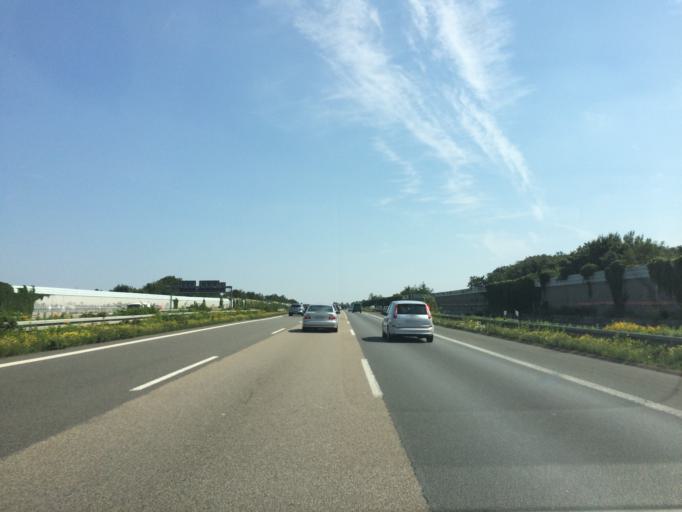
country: DE
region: North Rhine-Westphalia
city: Waltrop
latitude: 51.5839
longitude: 7.3908
